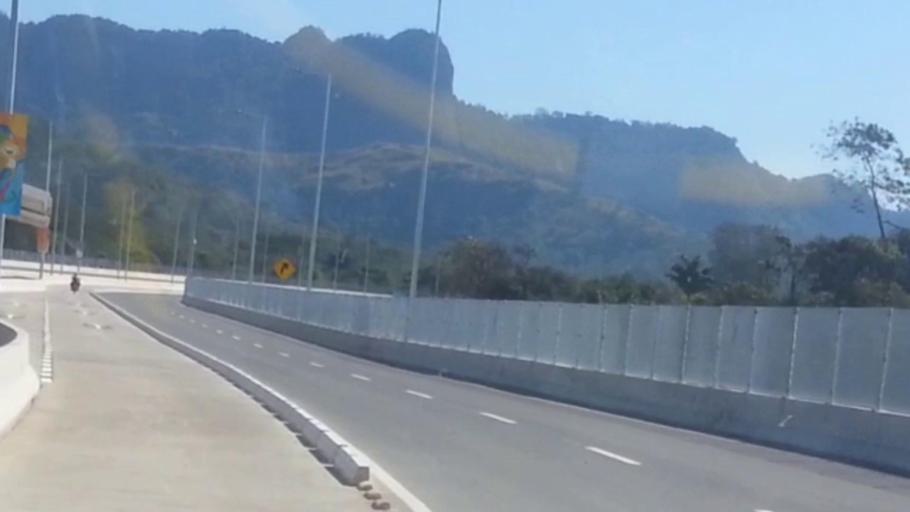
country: BR
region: Rio de Janeiro
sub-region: Nilopolis
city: Nilopolis
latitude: -22.9481
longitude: -43.3910
